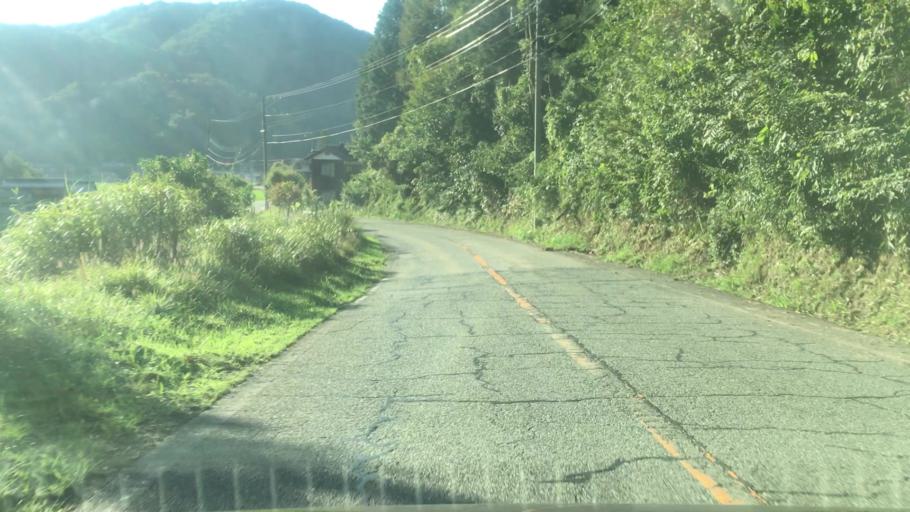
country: JP
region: Hyogo
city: Toyooka
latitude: 35.6207
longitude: 134.8689
